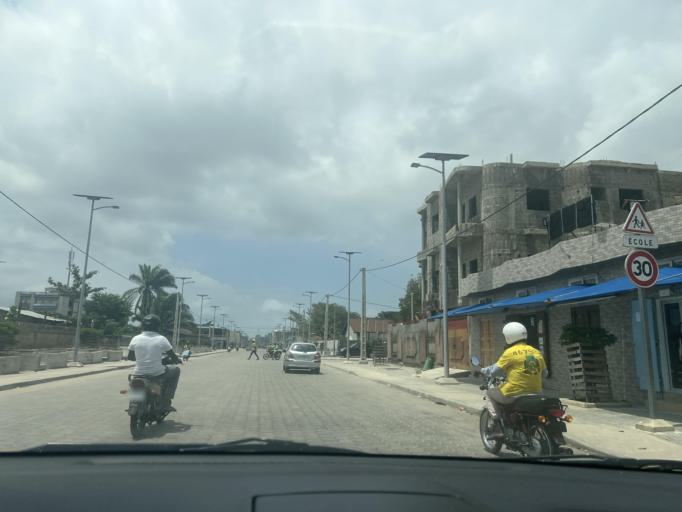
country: BJ
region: Littoral
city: Cotonou
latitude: 6.3845
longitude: 2.4509
